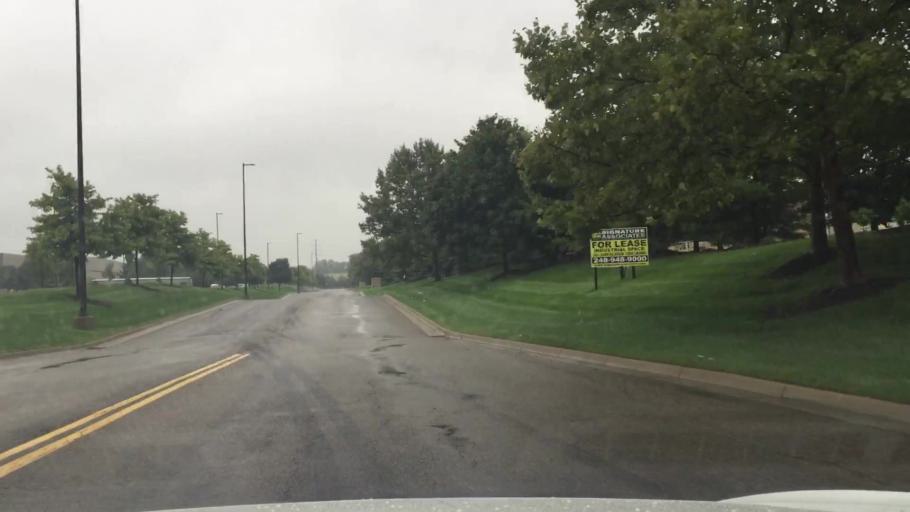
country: US
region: Michigan
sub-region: Wayne County
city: Livonia
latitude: 42.3818
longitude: -83.3268
